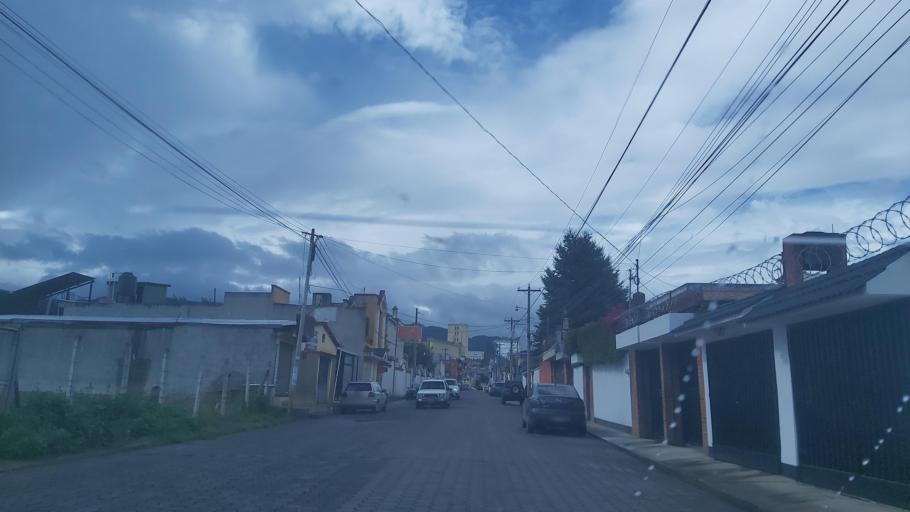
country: GT
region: Quetzaltenango
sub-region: Municipio de La Esperanza
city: La Esperanza
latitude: 14.8558
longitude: -91.5410
